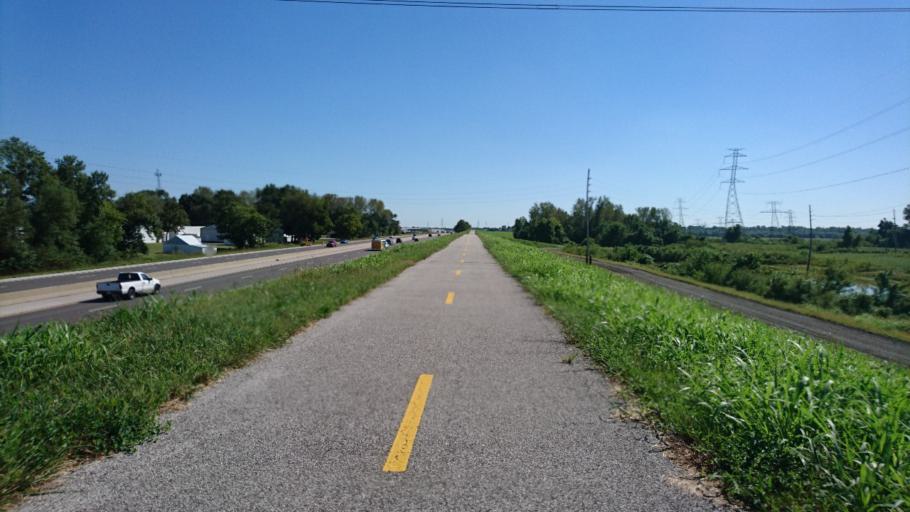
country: US
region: Illinois
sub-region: Madison County
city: Hartford
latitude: 38.8246
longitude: -90.1002
